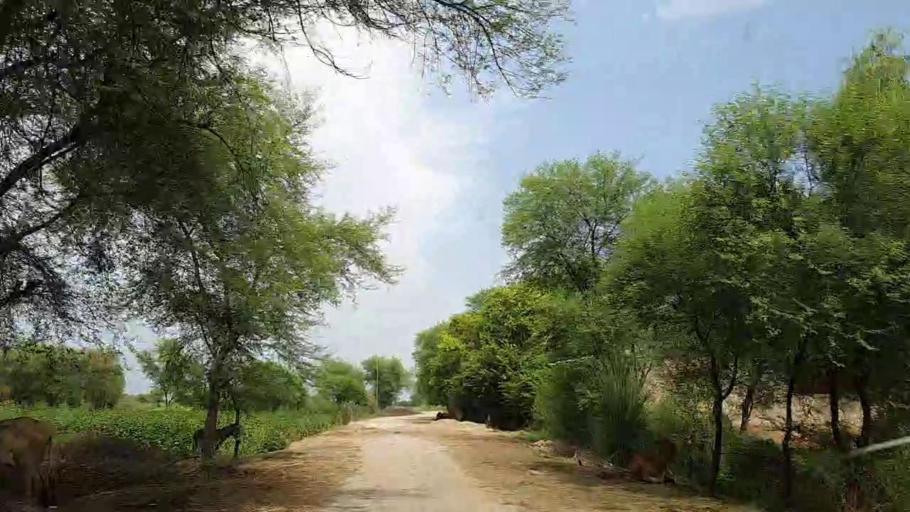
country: PK
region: Sindh
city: Khanpur
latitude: 27.8381
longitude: 69.4876
